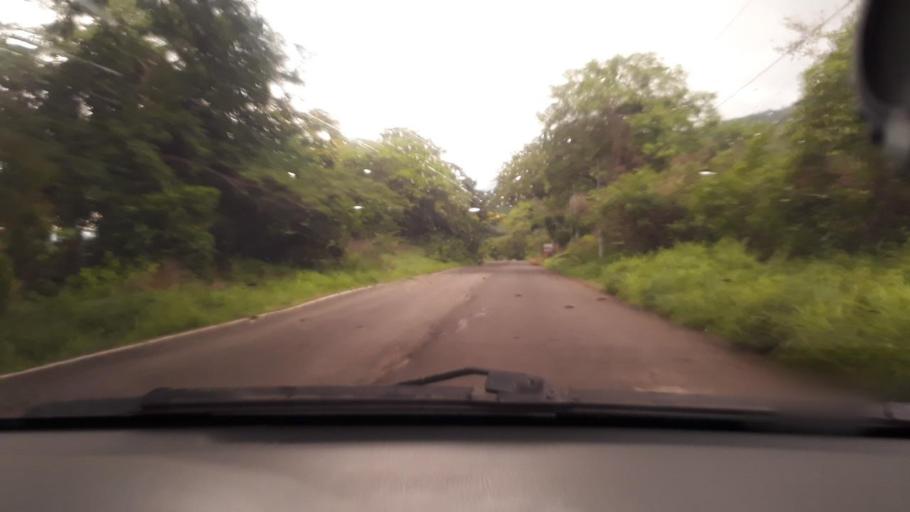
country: GT
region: Jutiapa
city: Comapa
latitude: 14.1029
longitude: -89.9636
